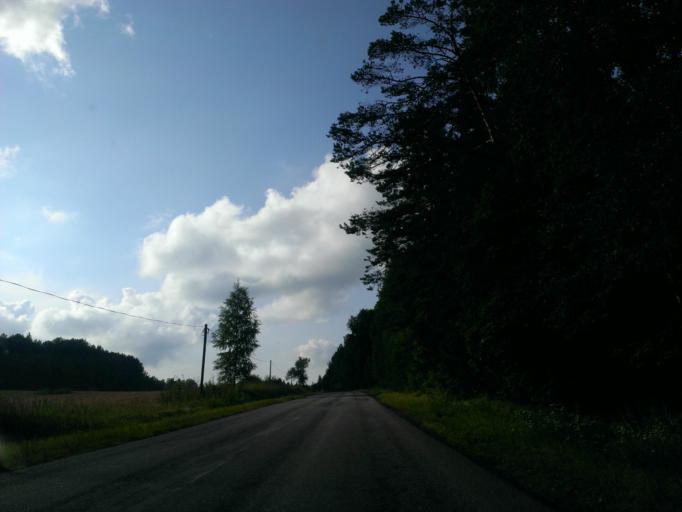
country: LV
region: Priekuli
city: Priekuli
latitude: 57.3120
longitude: 25.3811
